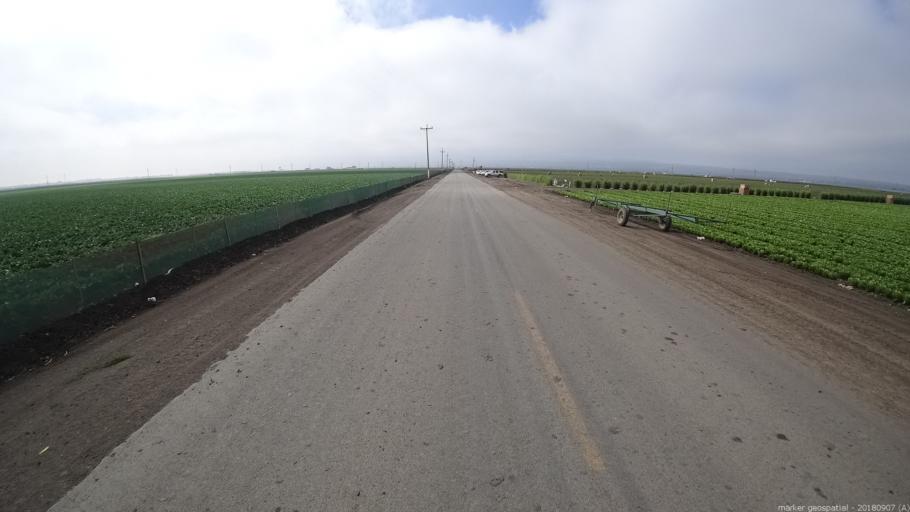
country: US
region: California
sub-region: Monterey County
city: Boronda
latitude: 36.6890
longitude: -121.7078
